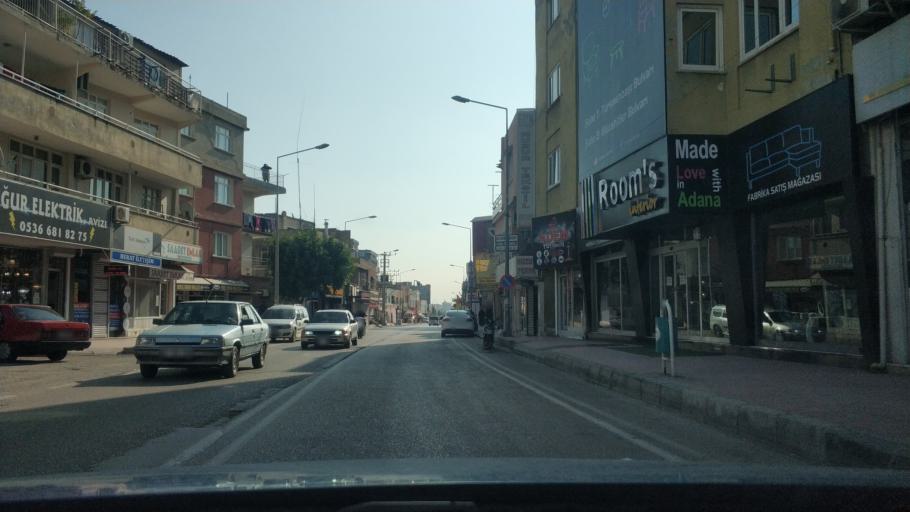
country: TR
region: Adana
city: Seyhan
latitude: 37.0186
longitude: 35.2979
